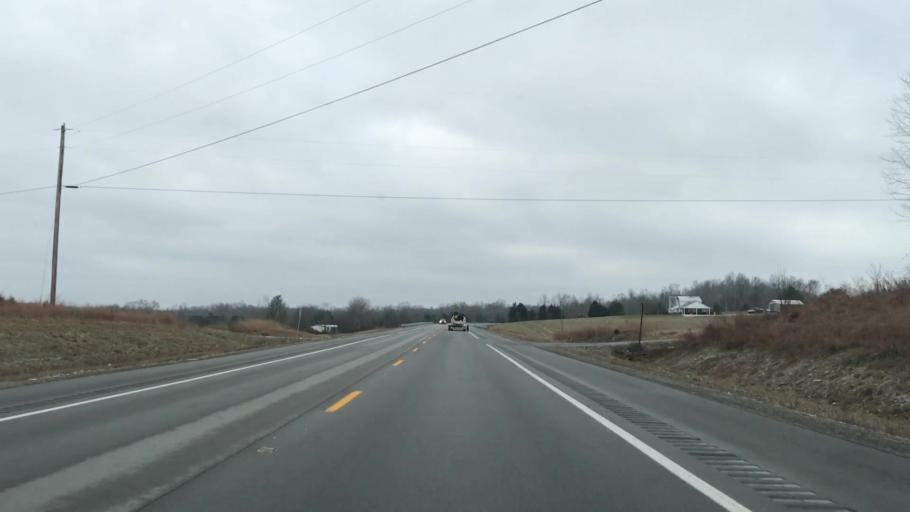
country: US
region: Kentucky
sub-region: Adair County
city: Columbia
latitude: 37.0562
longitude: -85.3602
